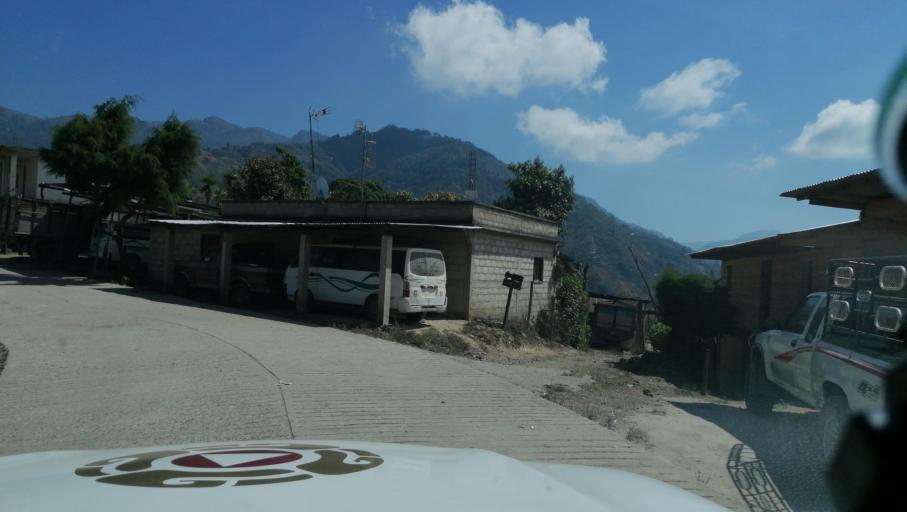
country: GT
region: San Marcos
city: Tacana
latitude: 15.2053
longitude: -92.2048
